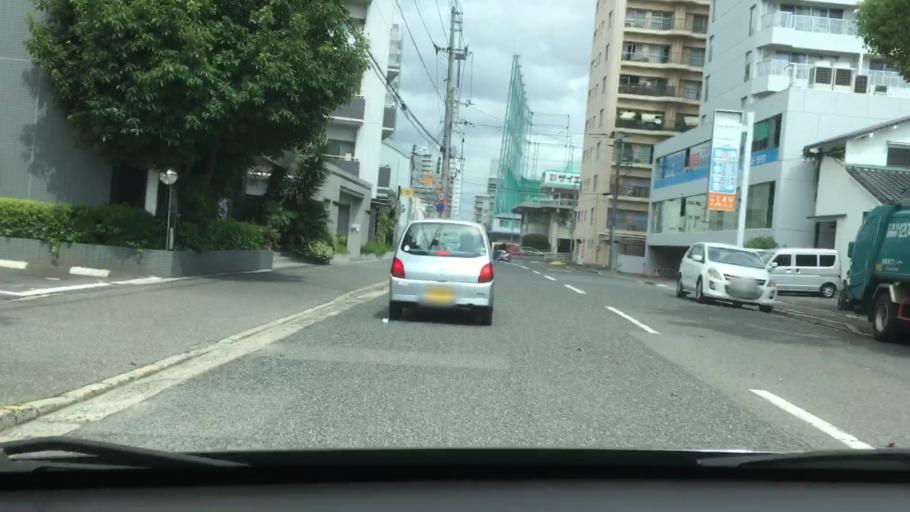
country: JP
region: Hiroshima
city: Hiroshima-shi
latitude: 34.3794
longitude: 132.4434
